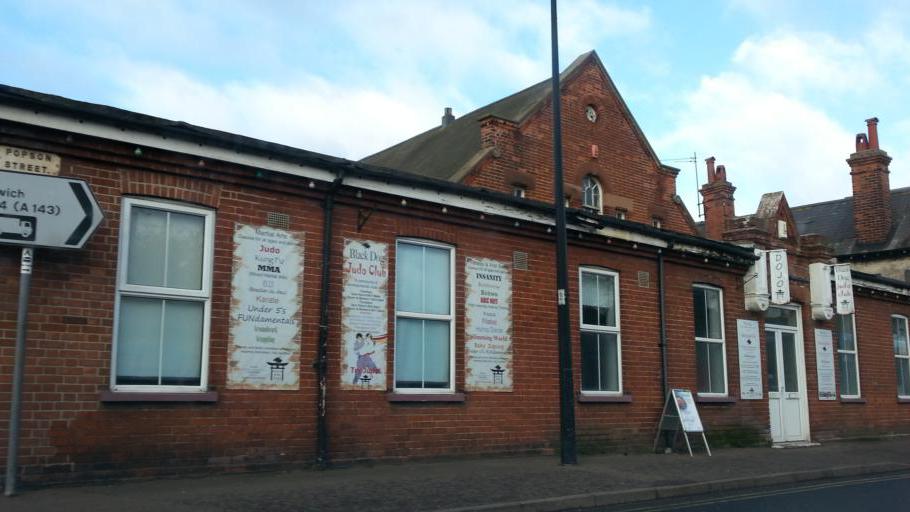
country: GB
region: England
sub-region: Suffolk
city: Bungay
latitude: 52.4573
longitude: 1.4346
